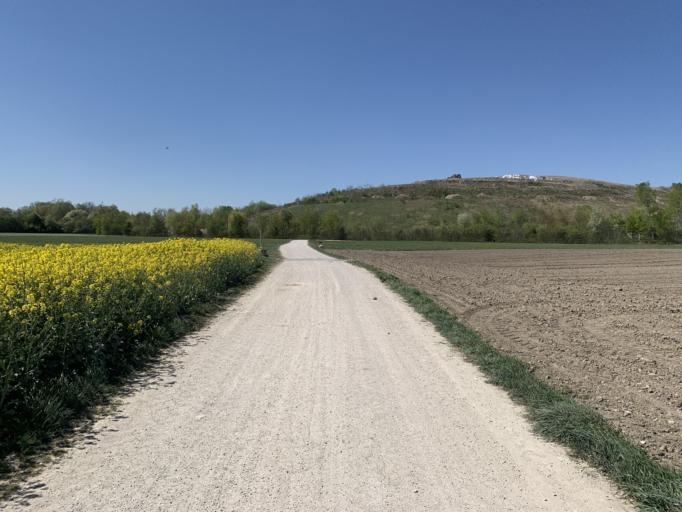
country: DE
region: Bavaria
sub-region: Swabia
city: Gersthofen
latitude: 48.4153
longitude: 10.9007
